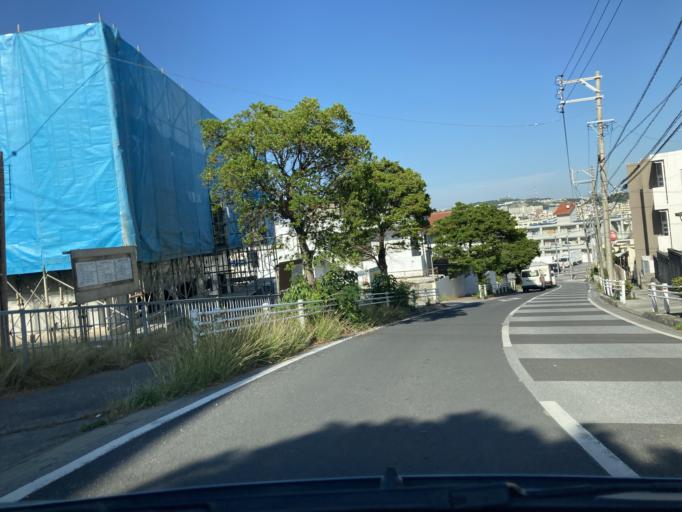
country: JP
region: Okinawa
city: Tomigusuku
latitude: 26.1793
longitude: 127.7063
